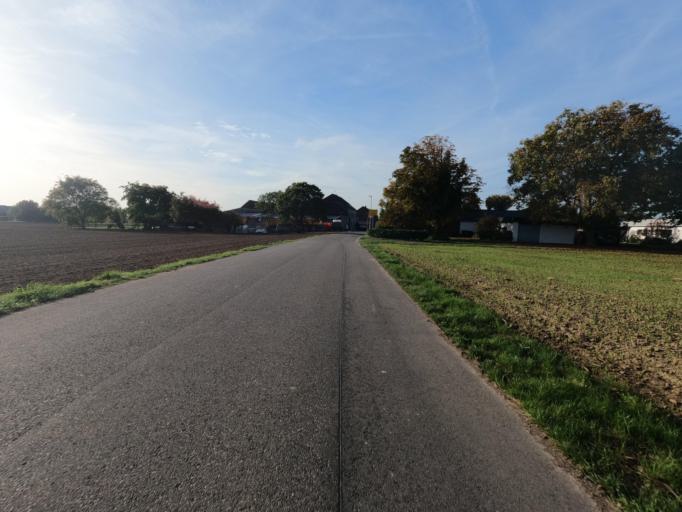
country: DE
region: North Rhine-Westphalia
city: Erkelenz
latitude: 51.0843
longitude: 6.3702
